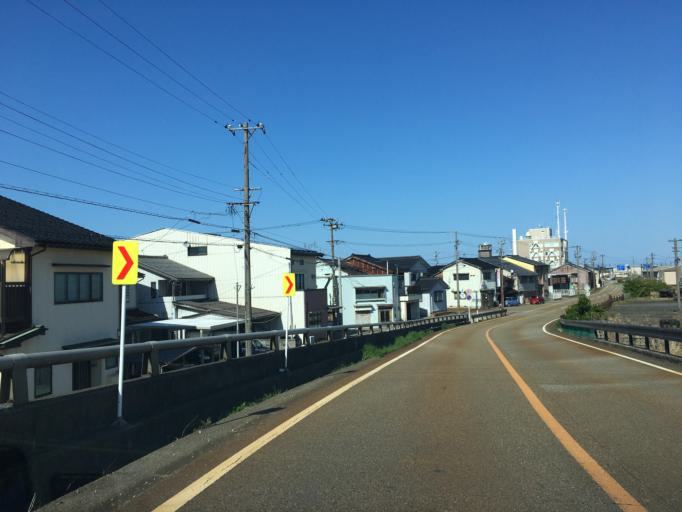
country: JP
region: Toyama
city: Nishishinminato
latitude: 36.7927
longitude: 137.0594
